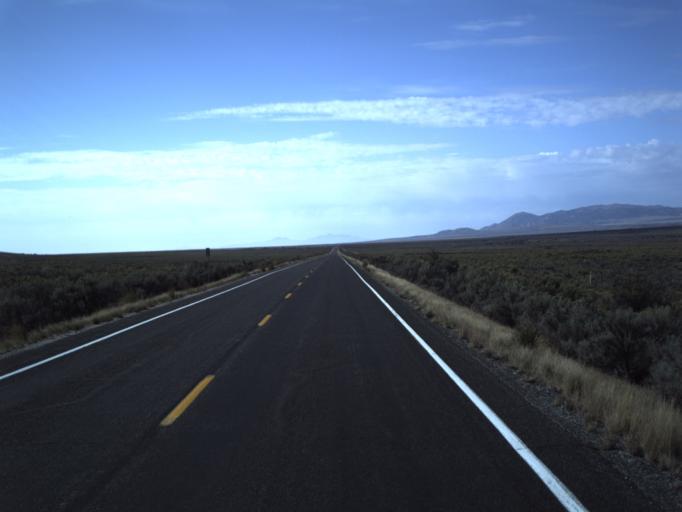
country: US
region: Idaho
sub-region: Cassia County
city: Burley
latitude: 41.6813
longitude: -113.5405
